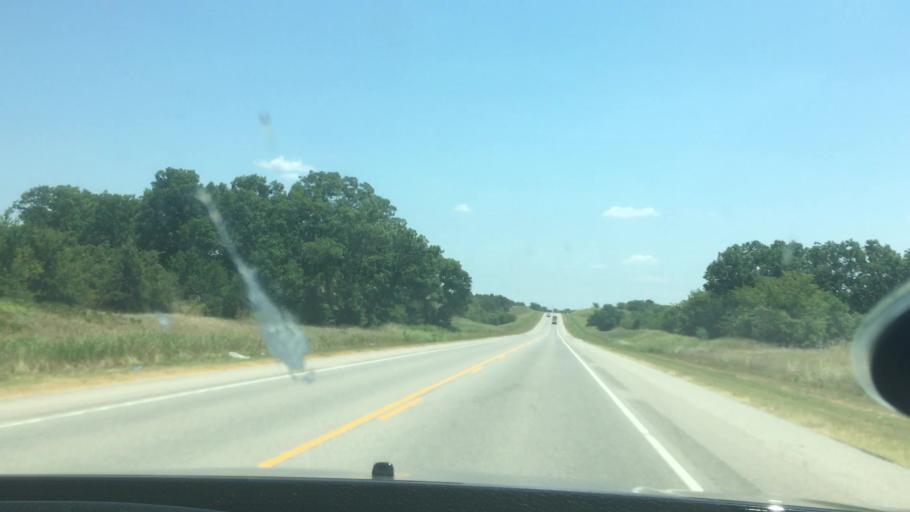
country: US
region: Oklahoma
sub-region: Pontotoc County
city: Ada
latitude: 34.6423
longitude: -96.5059
